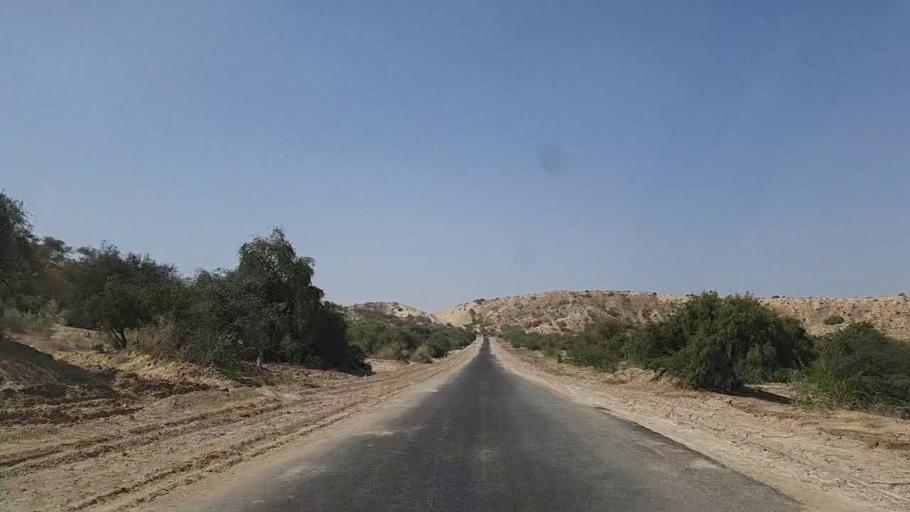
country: PK
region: Sindh
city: Diplo
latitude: 24.5846
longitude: 69.5229
